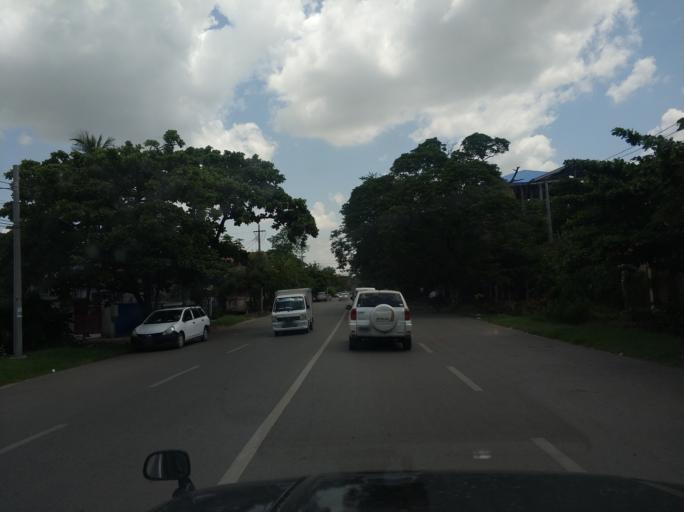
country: MM
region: Mandalay
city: Mandalay
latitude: 21.9794
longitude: 96.1036
